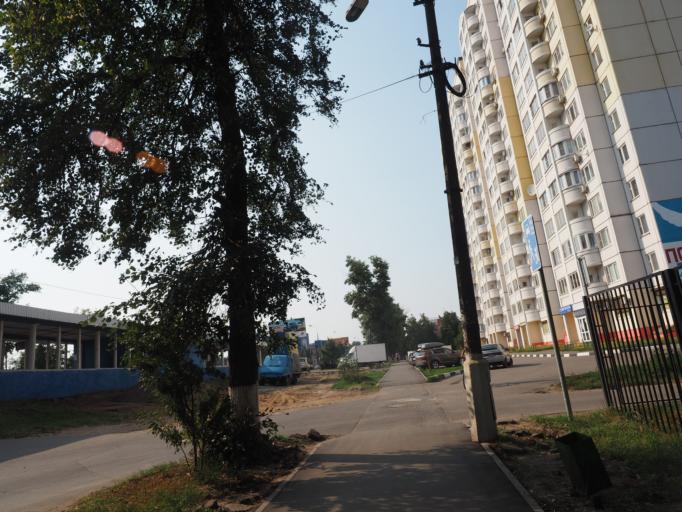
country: RU
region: Moskovskaya
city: Oktyabr'skiy
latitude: 55.6135
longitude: 37.9723
